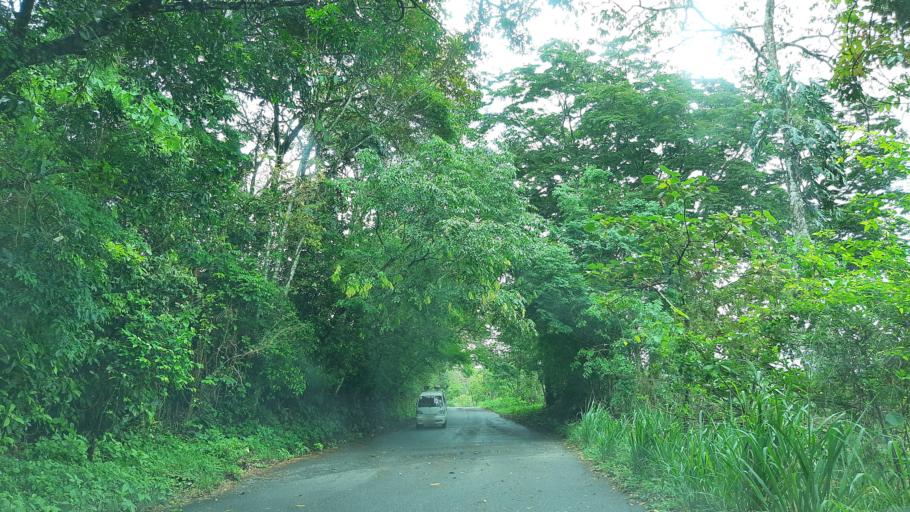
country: CO
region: Casanare
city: Sabanalarga
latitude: 4.8233
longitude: -73.0594
